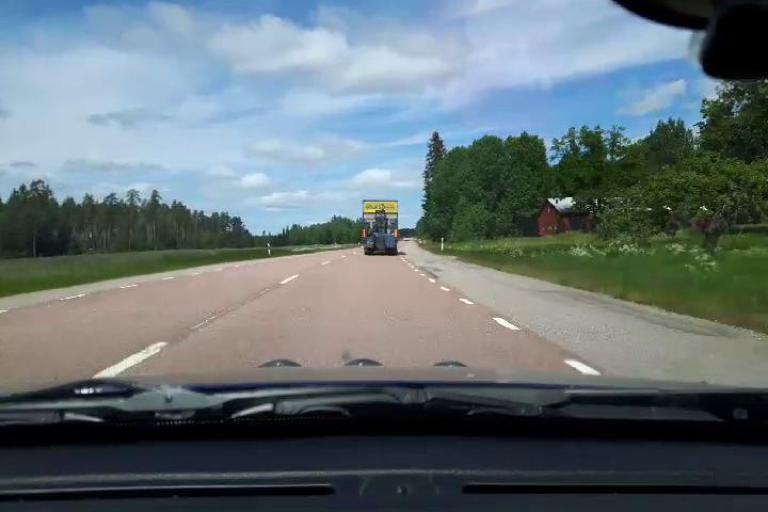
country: SE
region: Uppsala
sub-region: Osthammars Kommun
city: Bjorklinge
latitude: 60.1561
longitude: 17.4910
